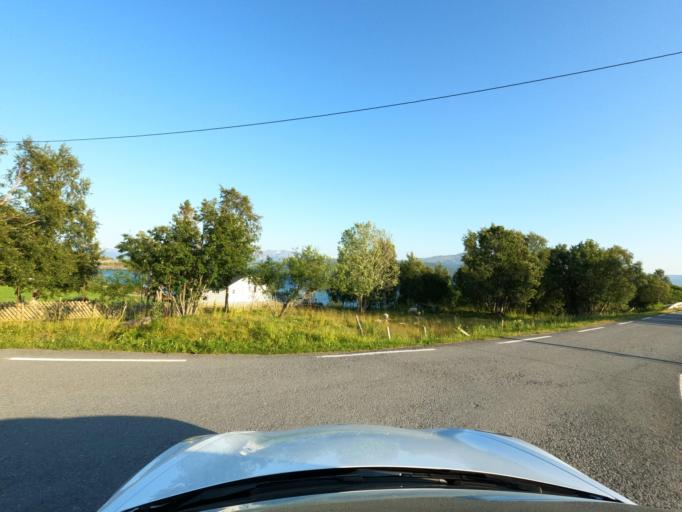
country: NO
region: Troms
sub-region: Skanland
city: Evenskjer
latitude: 68.4589
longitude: 16.6956
